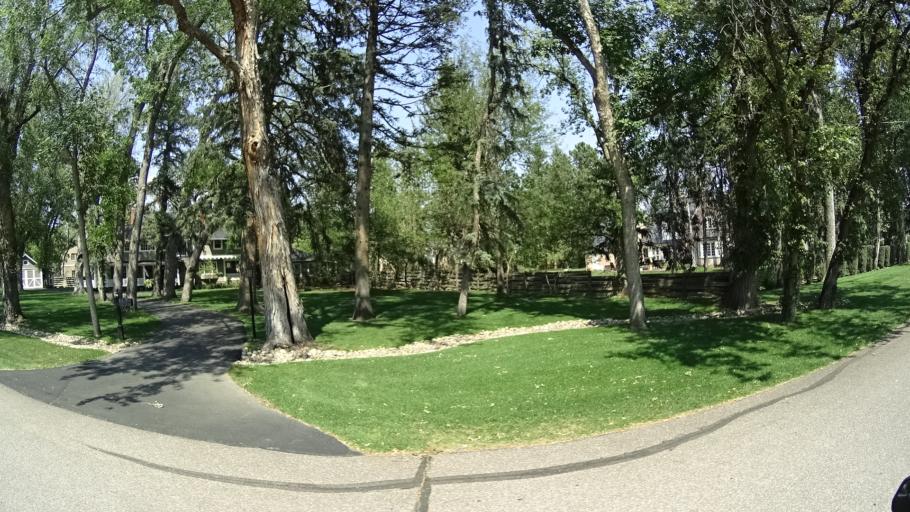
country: US
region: Colorado
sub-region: El Paso County
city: Colorado Springs
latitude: 38.7903
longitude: -104.8457
